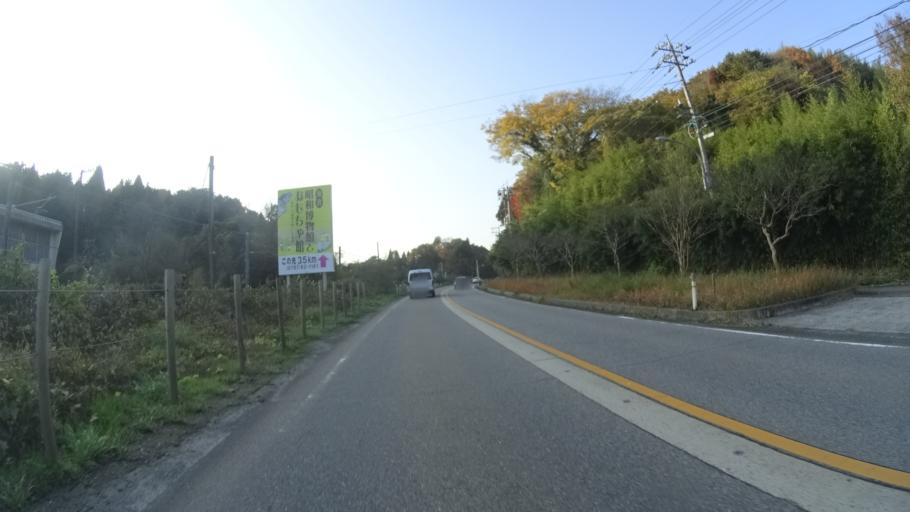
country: JP
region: Ishikawa
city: Nanao
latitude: 37.0576
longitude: 136.9484
